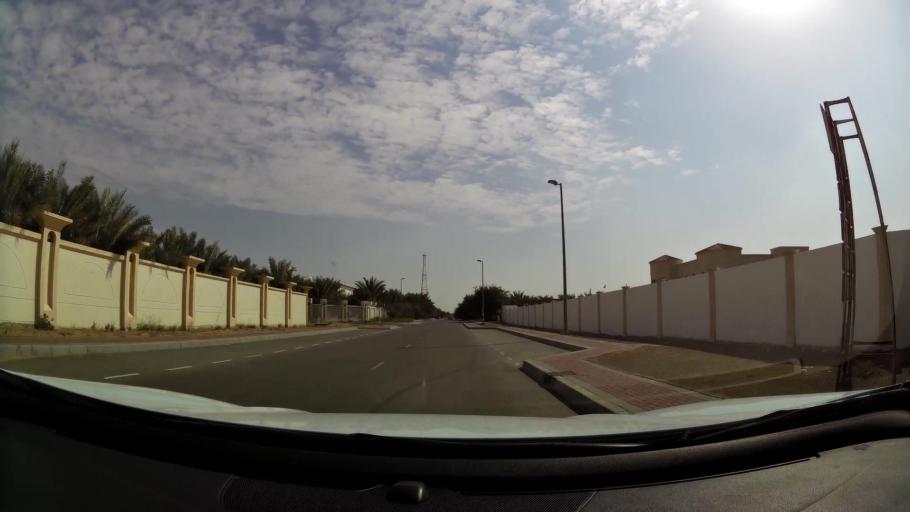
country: AE
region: Abu Dhabi
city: Al Ain
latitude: 24.1000
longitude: 55.9138
